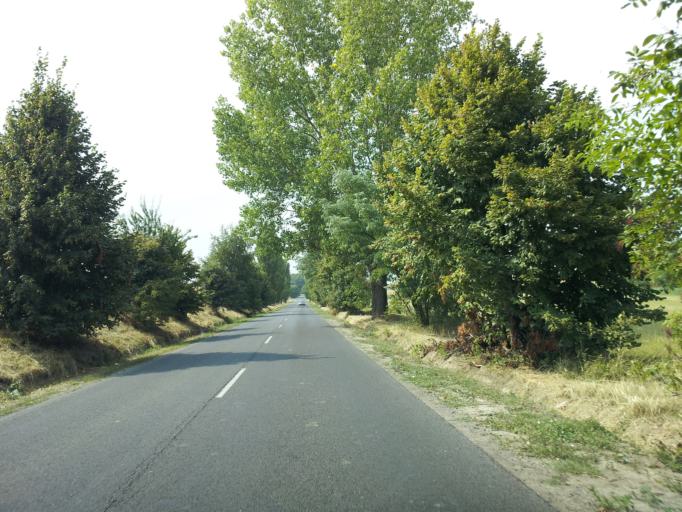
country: HU
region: Gyor-Moson-Sopron
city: Pannonhalma
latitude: 47.5578
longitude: 17.7405
